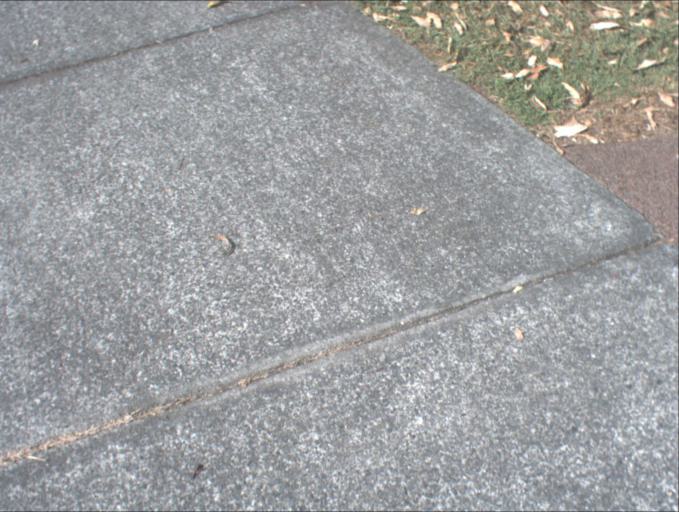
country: AU
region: Queensland
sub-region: Logan
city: Beenleigh
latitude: -27.7054
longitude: 153.1984
